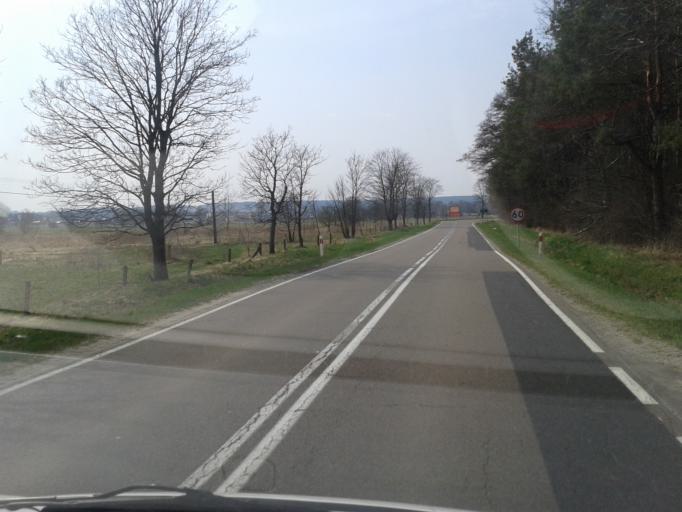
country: PL
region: Subcarpathian Voivodeship
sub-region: Powiat lubaczowski
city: Narol
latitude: 50.3607
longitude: 23.3392
